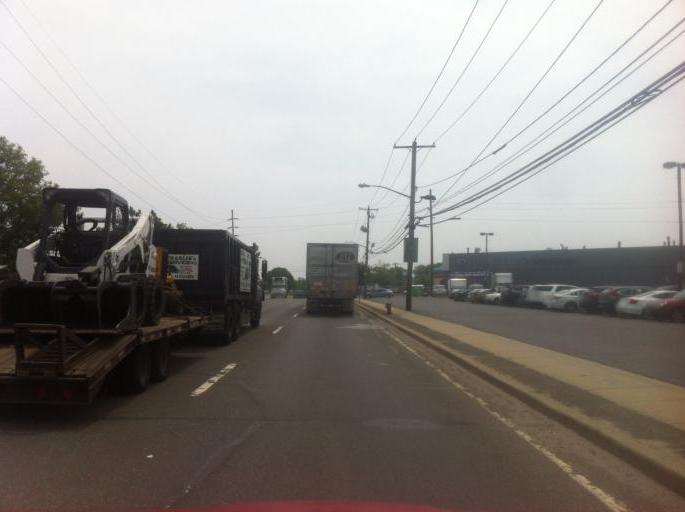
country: US
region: New York
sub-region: Nassau County
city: Bethpage
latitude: 40.7454
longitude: -73.4998
